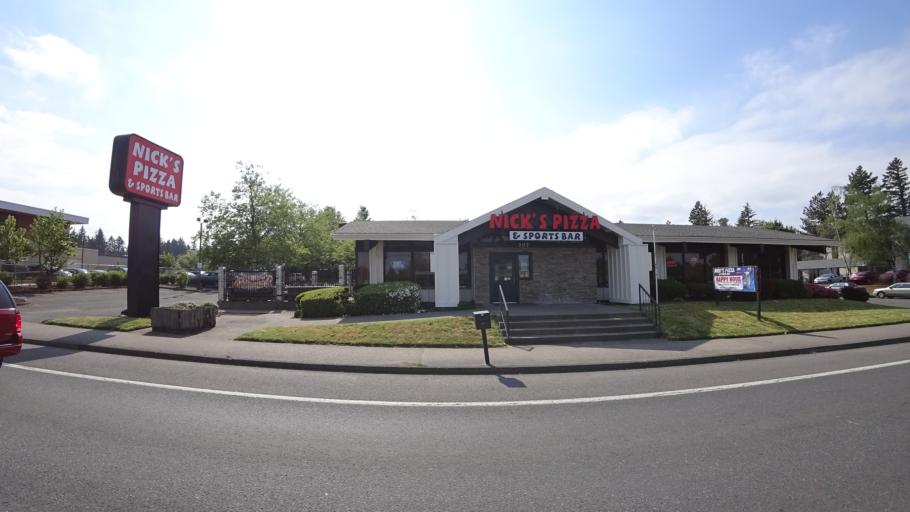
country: US
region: Oregon
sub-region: Multnomah County
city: Fairview
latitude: 45.5279
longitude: -122.4770
